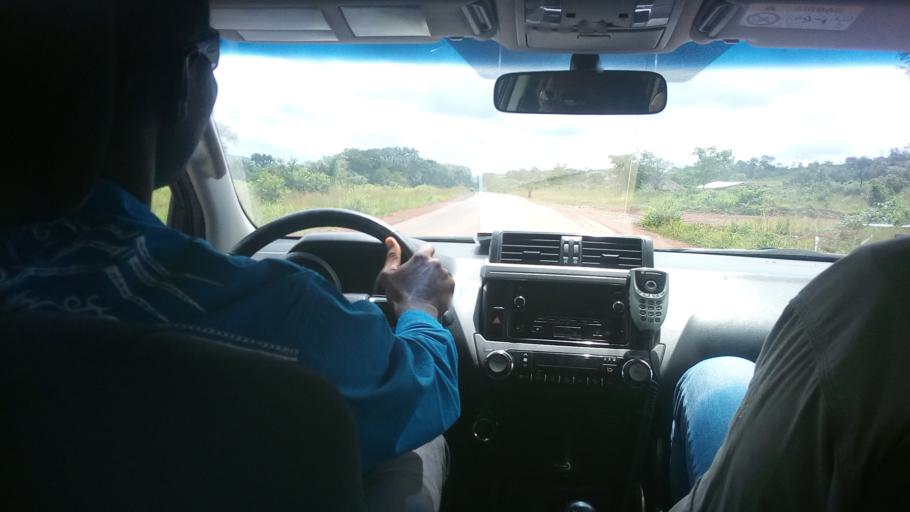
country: GN
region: Boke
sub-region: Boke Prefecture
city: Boke
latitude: 11.0231
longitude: -14.0666
